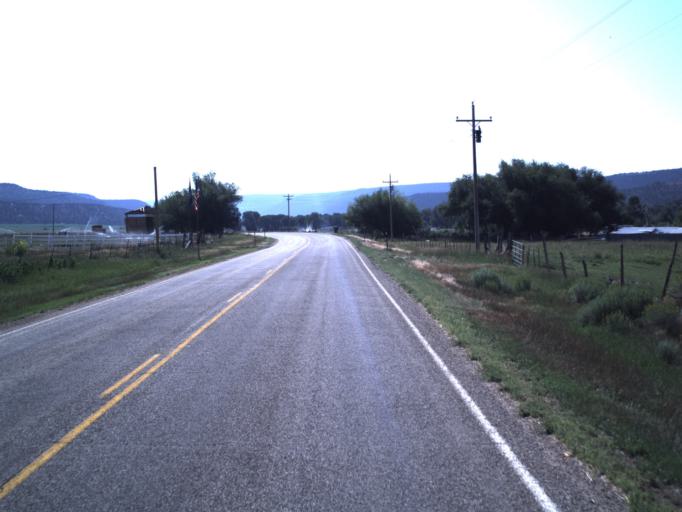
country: US
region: Utah
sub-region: Duchesne County
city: Duchesne
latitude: 40.3447
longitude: -110.6987
